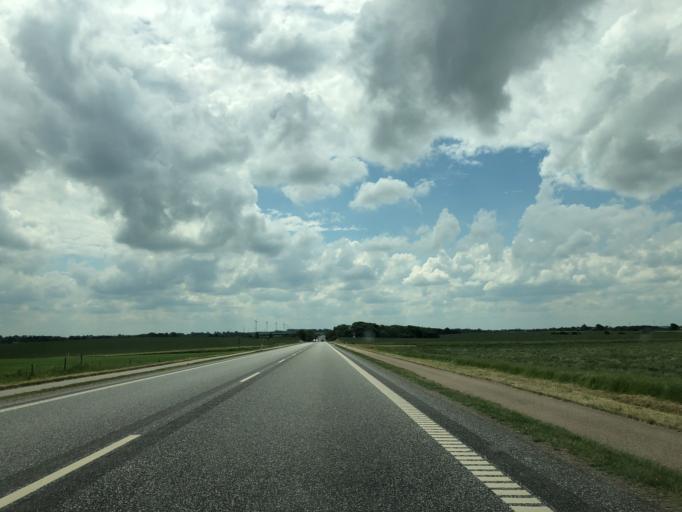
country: DK
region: Central Jutland
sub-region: Struer Kommune
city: Struer
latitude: 56.4662
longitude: 8.5881
